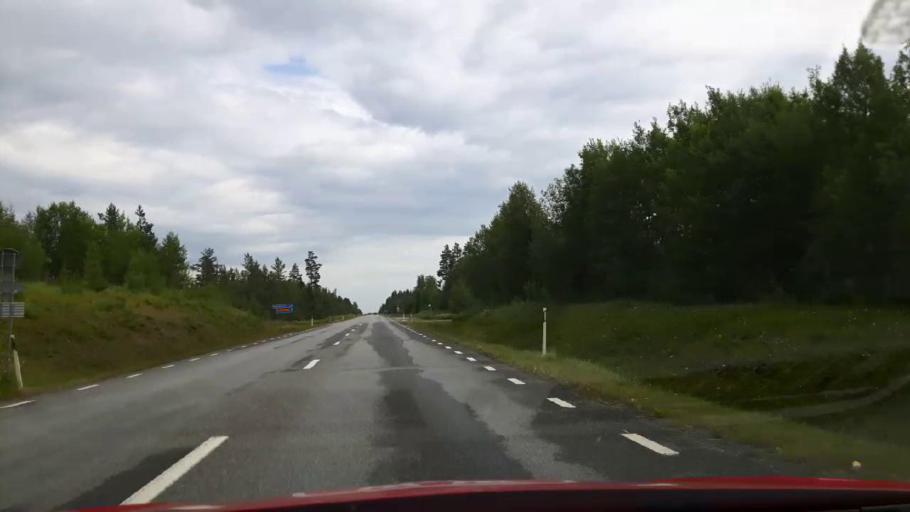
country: SE
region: Jaemtland
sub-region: Stroemsunds Kommun
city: Stroemsund
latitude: 63.6939
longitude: 15.4266
